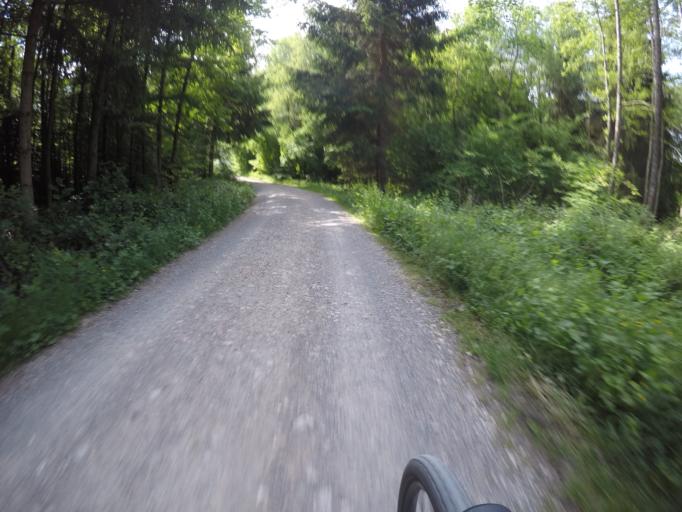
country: DE
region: Baden-Wuerttemberg
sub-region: Regierungsbezirk Stuttgart
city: Denkendorf
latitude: 48.6714
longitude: 9.3157
